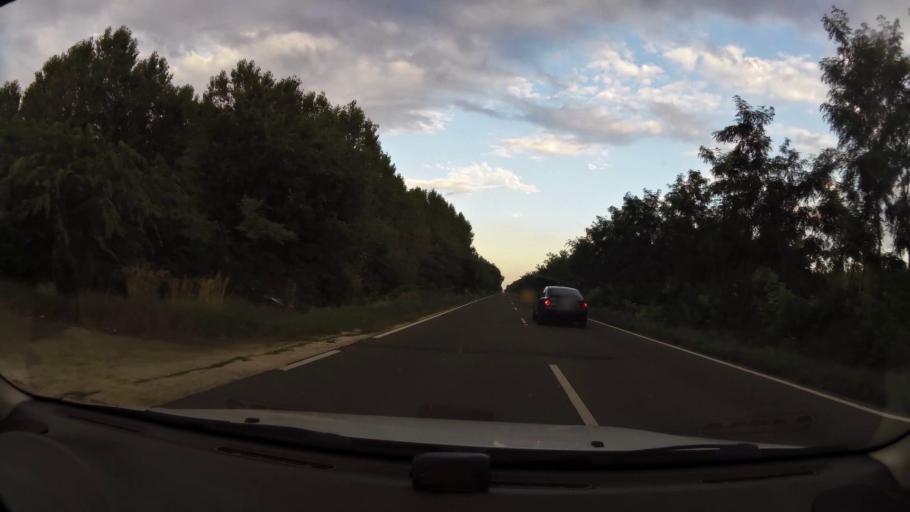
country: HU
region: Pest
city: Ujszilvas
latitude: 47.2988
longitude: 19.8928
